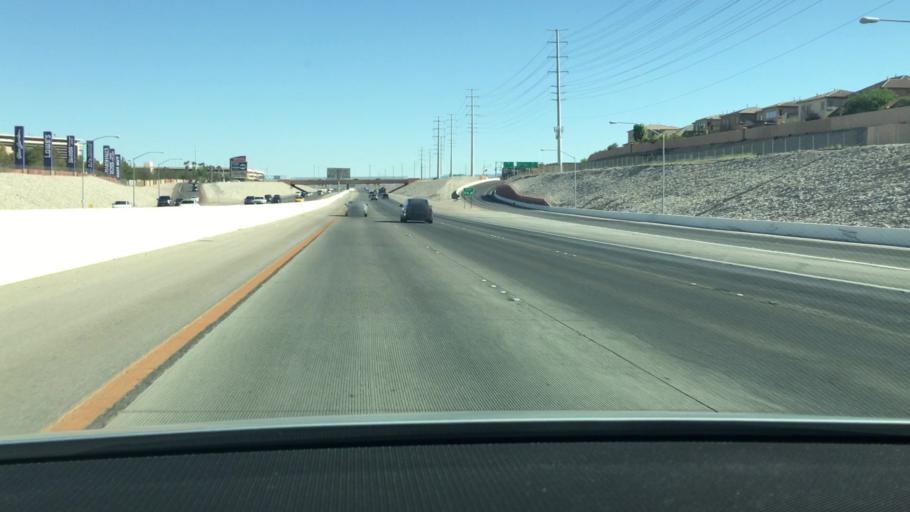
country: US
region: Nevada
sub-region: Clark County
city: Summerlin South
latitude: 36.1646
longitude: -115.3375
